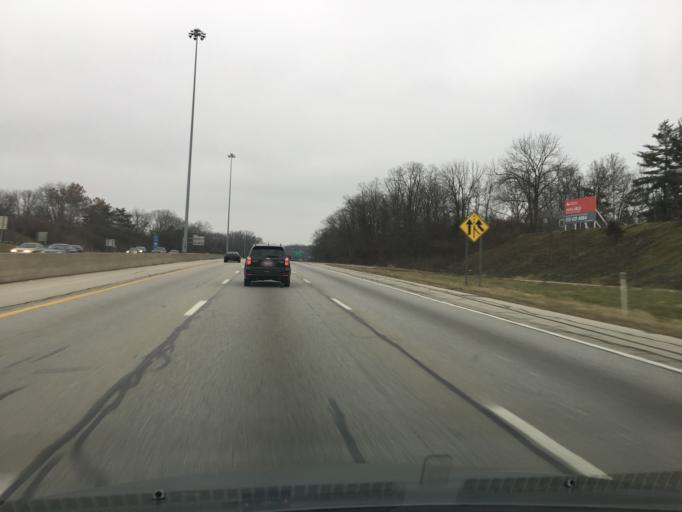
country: US
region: Ohio
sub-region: Hamilton County
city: Sharonville
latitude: 39.2895
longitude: -84.3938
